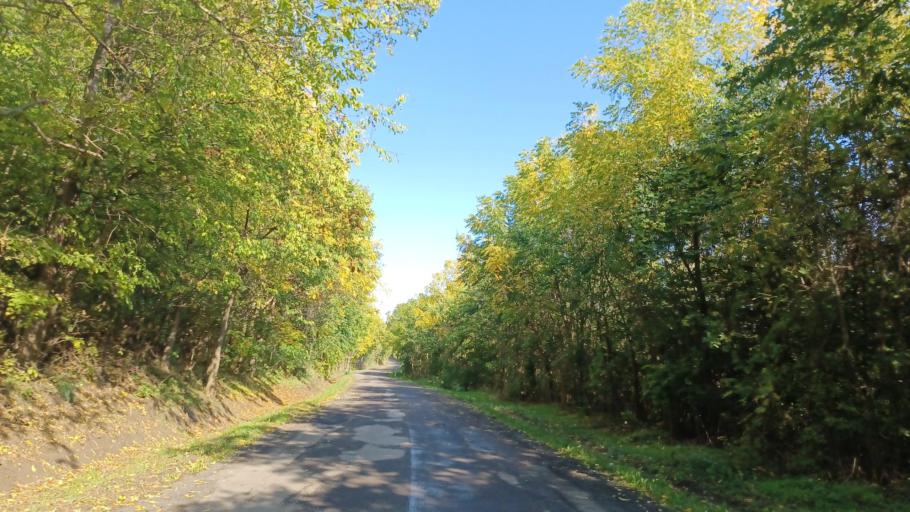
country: HU
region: Tolna
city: Szedres
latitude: 46.5343
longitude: 18.5930
